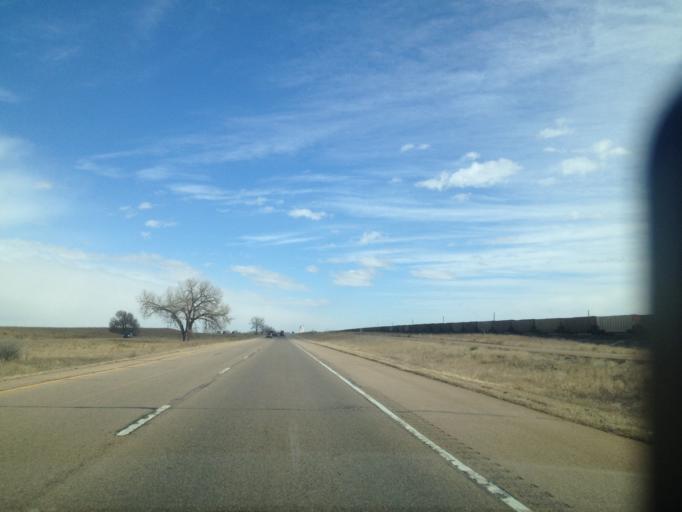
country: US
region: Colorado
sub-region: Weld County
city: Keenesburg
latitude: 40.1669
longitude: -104.4080
